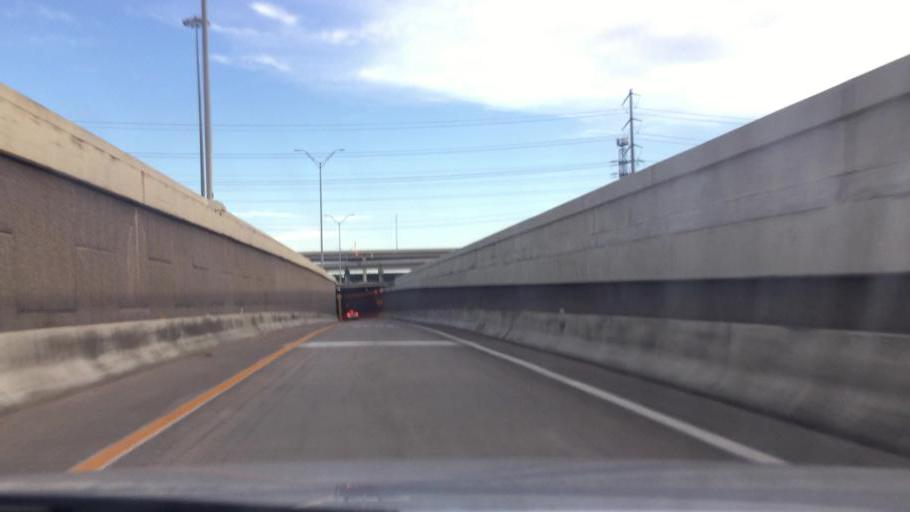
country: US
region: Texas
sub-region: Harris County
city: Bunker Hill Village
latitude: 29.7210
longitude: -95.5575
